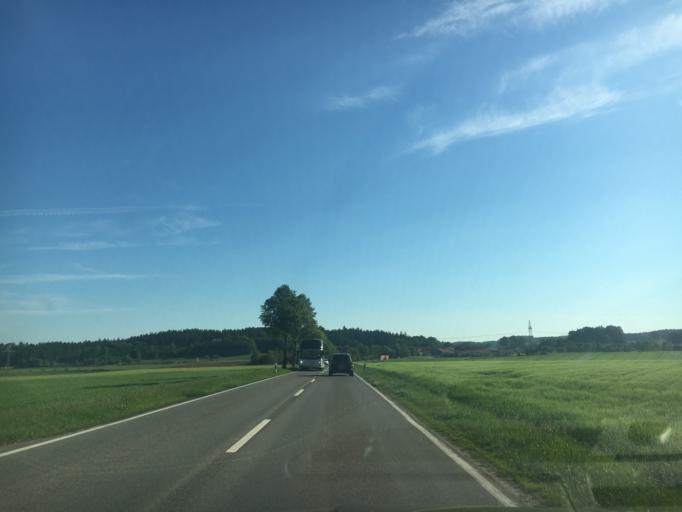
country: DE
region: Bavaria
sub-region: Upper Bavaria
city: Chieming
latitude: 47.8968
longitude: 12.5446
